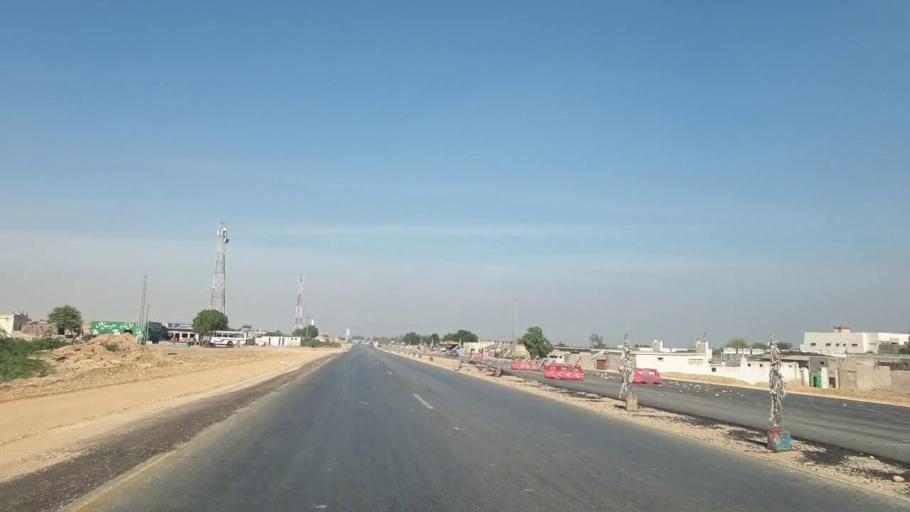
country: PK
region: Sindh
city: Hala
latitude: 25.7000
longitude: 68.2956
